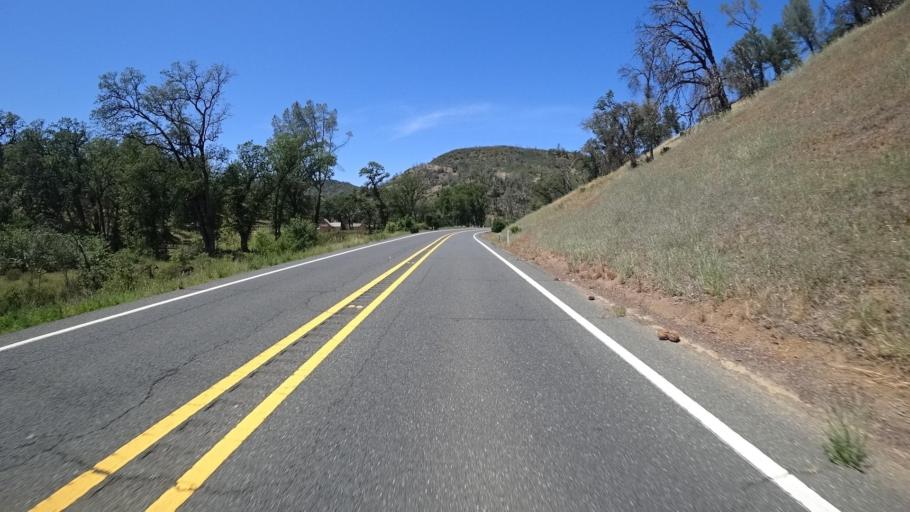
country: US
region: California
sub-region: Lake County
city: Lower Lake
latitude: 38.8570
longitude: -122.6255
